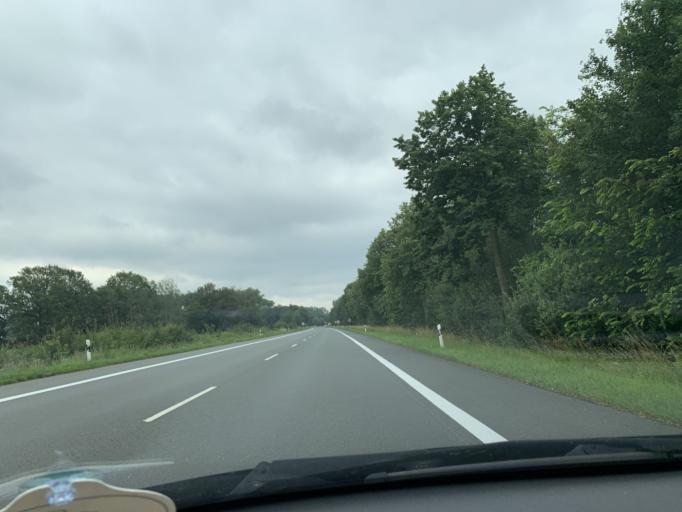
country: DE
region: North Rhine-Westphalia
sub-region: Regierungsbezirk Munster
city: Ennigerloh
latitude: 51.9061
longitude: 8.0500
